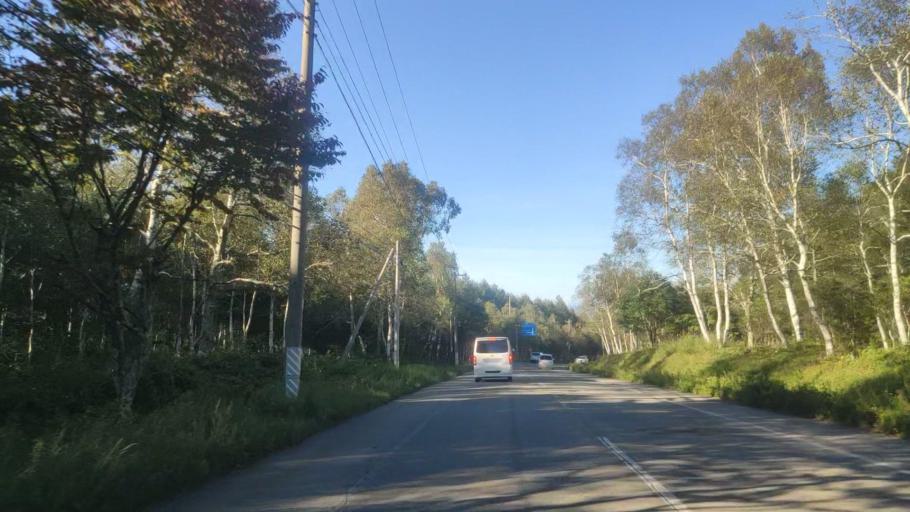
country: JP
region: Nagano
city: Kamimaruko
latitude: 36.1671
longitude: 138.2804
